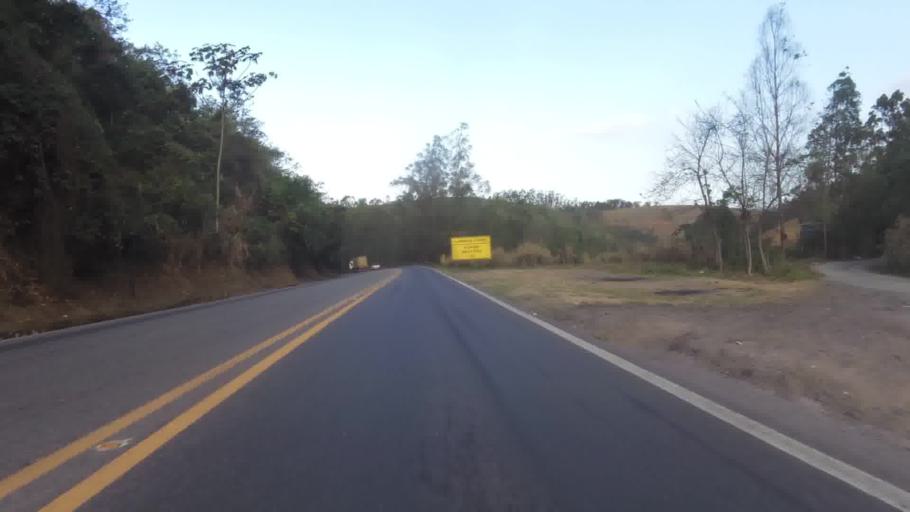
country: BR
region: Espirito Santo
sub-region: Rio Novo Do Sul
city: Rio Novo do Sul
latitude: -20.8656
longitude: -40.9275
